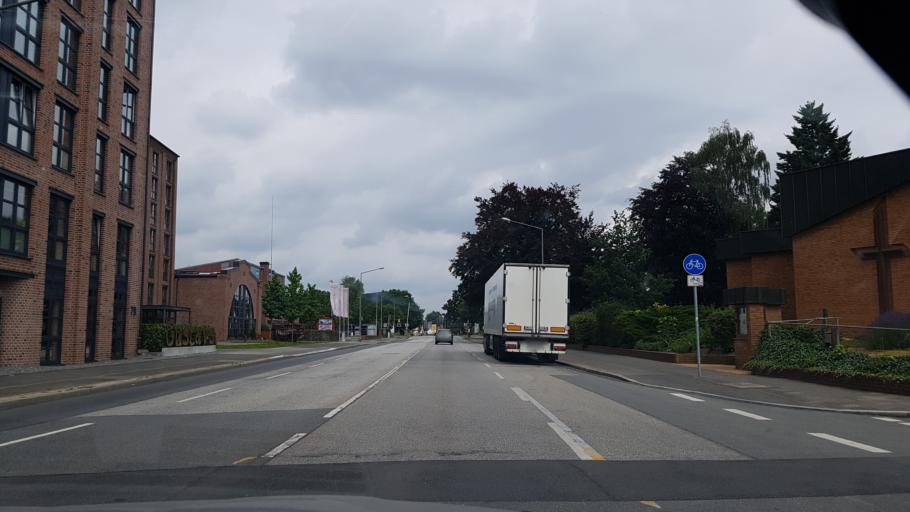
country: DE
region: Schleswig-Holstein
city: Neumunster
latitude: 54.0826
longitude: 9.9791
